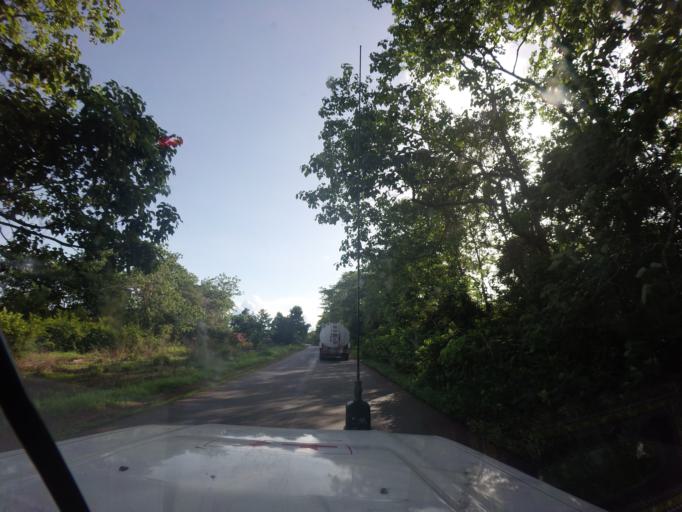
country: GN
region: Kindia
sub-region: Kindia
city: Kindia
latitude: 10.0050
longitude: -12.7013
